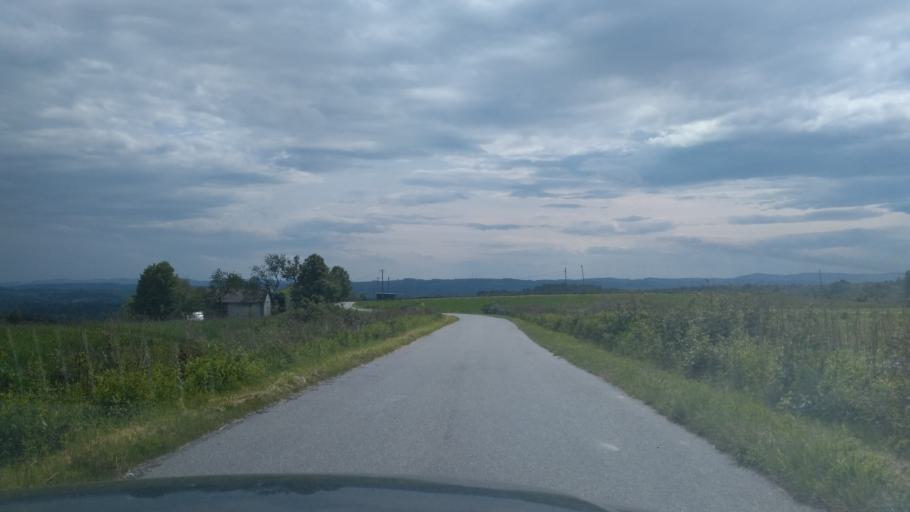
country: PL
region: Subcarpathian Voivodeship
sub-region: Powiat ropczycko-sedziszowski
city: Zagorzyce
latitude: 49.9756
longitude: 21.6592
